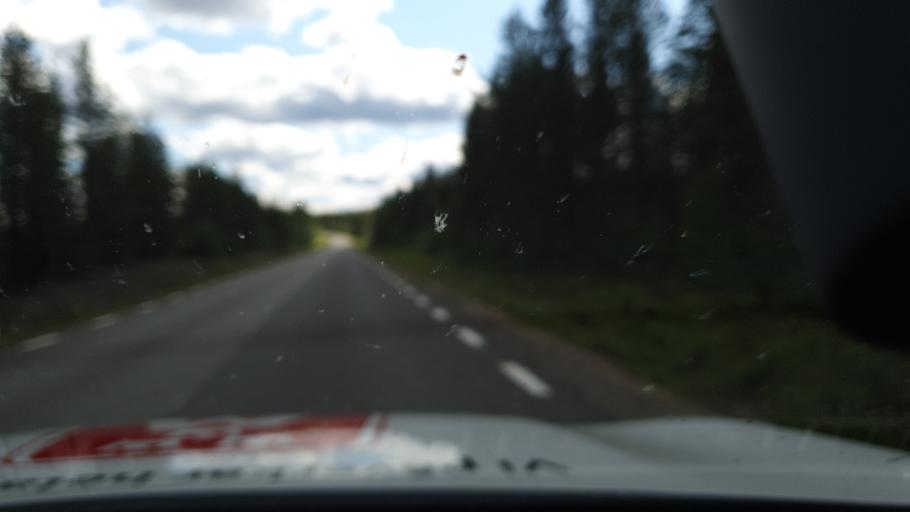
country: SE
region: Norrbotten
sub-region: Arjeplogs Kommun
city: Arjeplog
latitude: 65.5706
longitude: 18.1751
